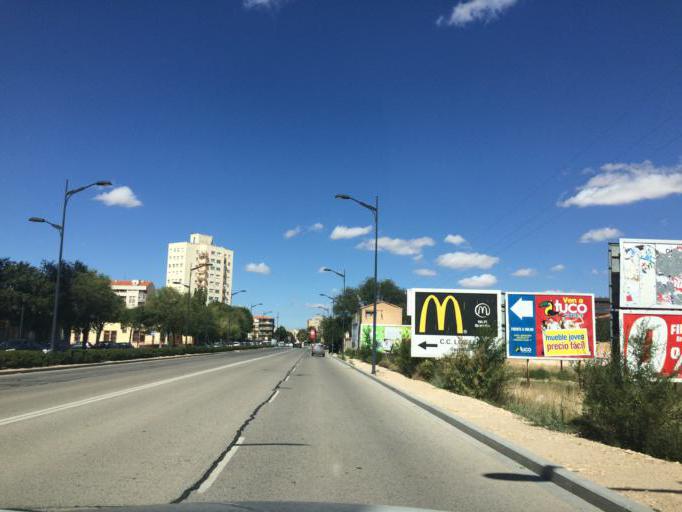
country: ES
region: Castille-La Mancha
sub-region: Provincia de Albacete
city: Albacete
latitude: 38.9819
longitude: -1.8471
